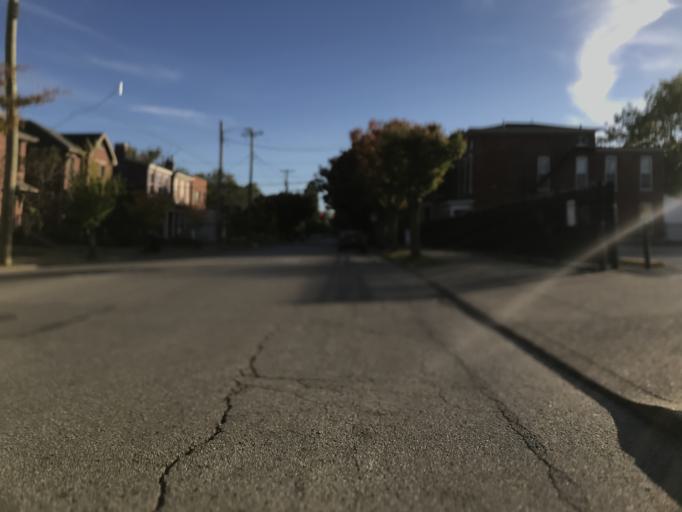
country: US
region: Kentucky
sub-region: Jefferson County
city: Louisville
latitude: 38.2364
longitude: -85.7635
